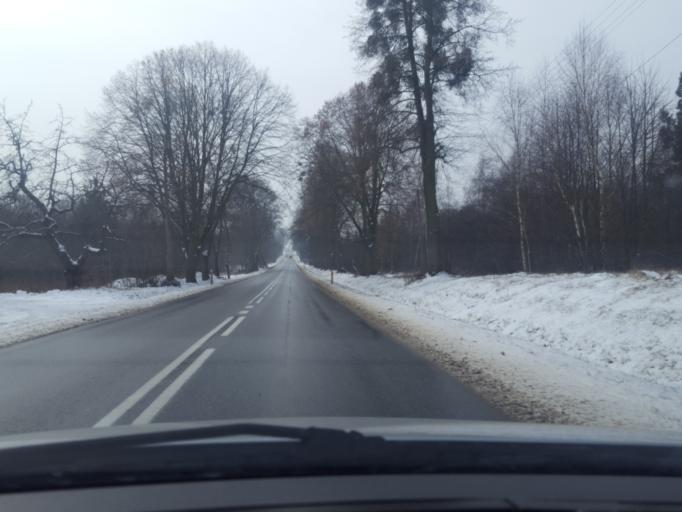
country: PL
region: Lodz Voivodeship
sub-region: Powiat brzezinski
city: Brzeziny
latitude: 51.8226
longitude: 19.7761
